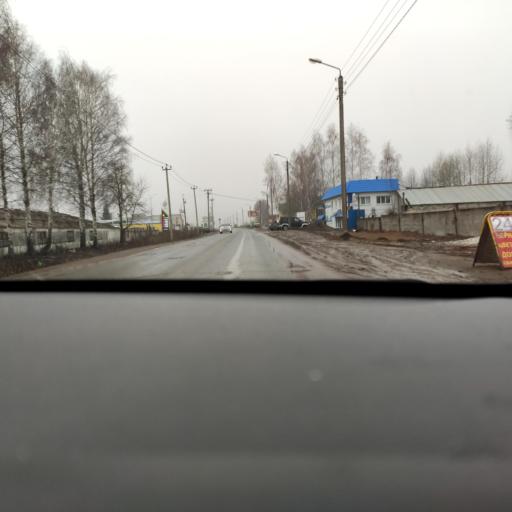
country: RU
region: Tatarstan
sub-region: Chistopol'skiy Rayon
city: Chistopol'
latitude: 55.3491
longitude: 50.6639
